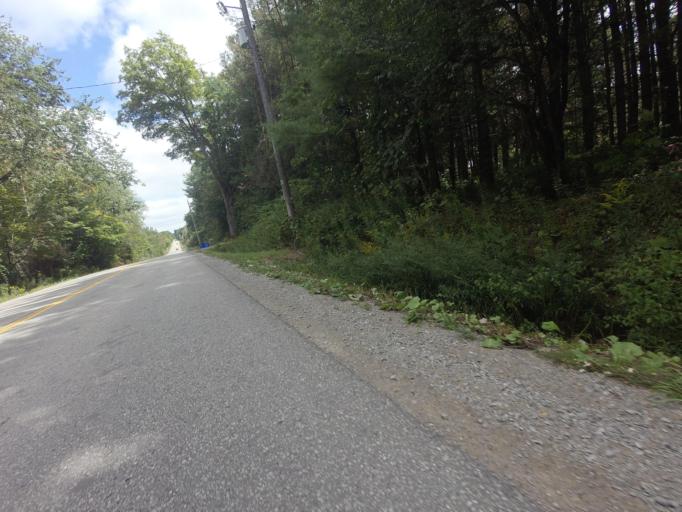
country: CA
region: Ontario
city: Uxbridge
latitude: 44.1231
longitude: -79.1773
